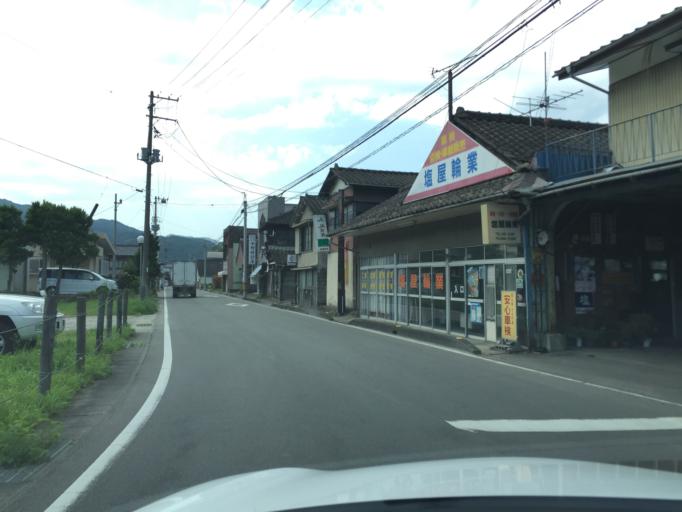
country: JP
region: Fukushima
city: Iwaki
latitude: 37.0347
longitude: 140.7094
